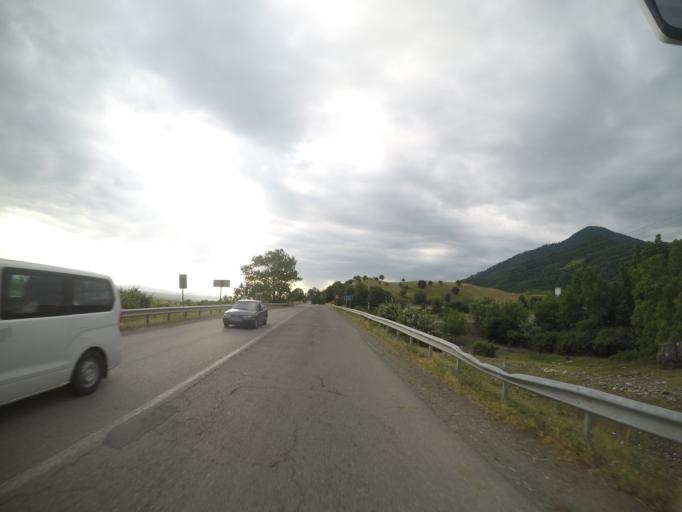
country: AZ
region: Ismayilli
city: Ismayilli
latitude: 40.8459
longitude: 48.1425
